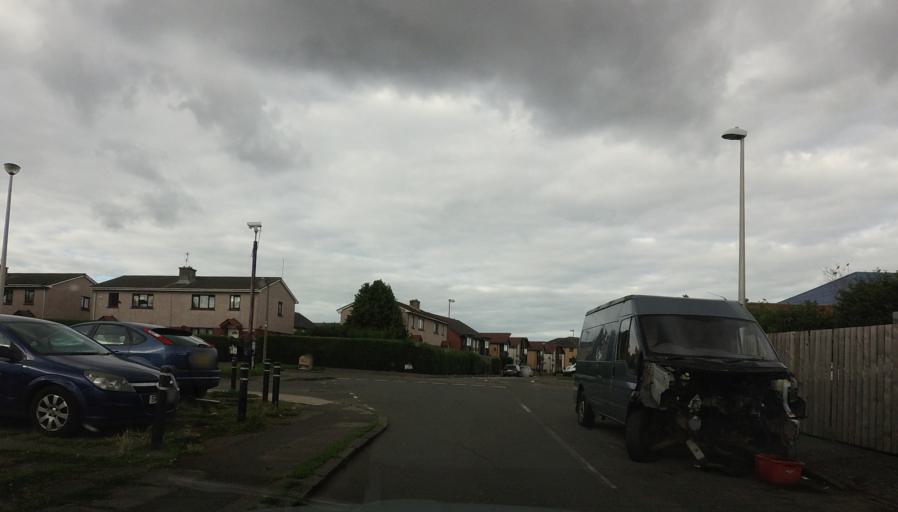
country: GB
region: Scotland
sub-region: Midlothian
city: Loanhead
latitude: 55.8982
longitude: -3.1570
